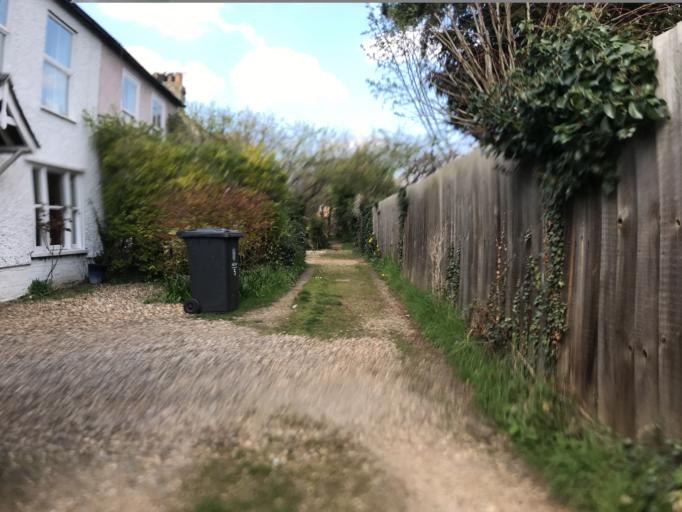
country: GB
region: England
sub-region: Cambridgeshire
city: Sawston
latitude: 52.1514
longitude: 0.1420
